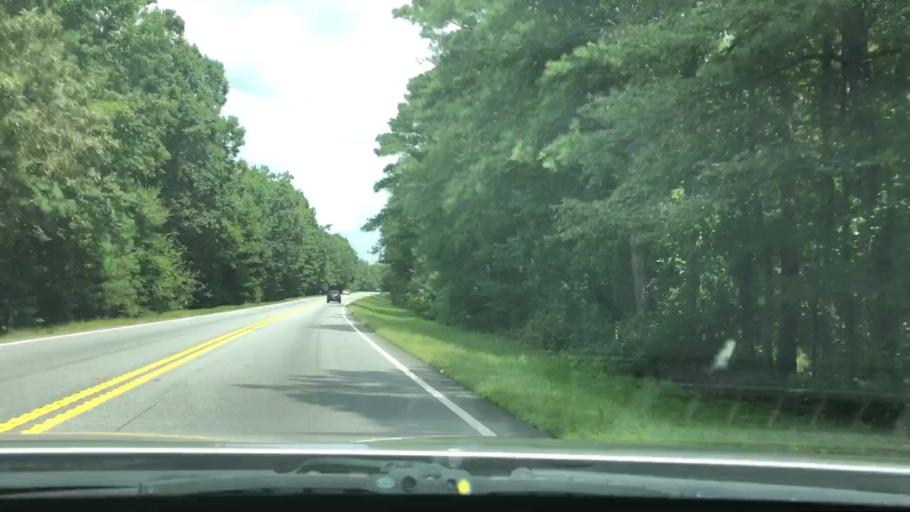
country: US
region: Georgia
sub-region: Lamar County
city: Barnesville
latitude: 33.1636
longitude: -84.1043
